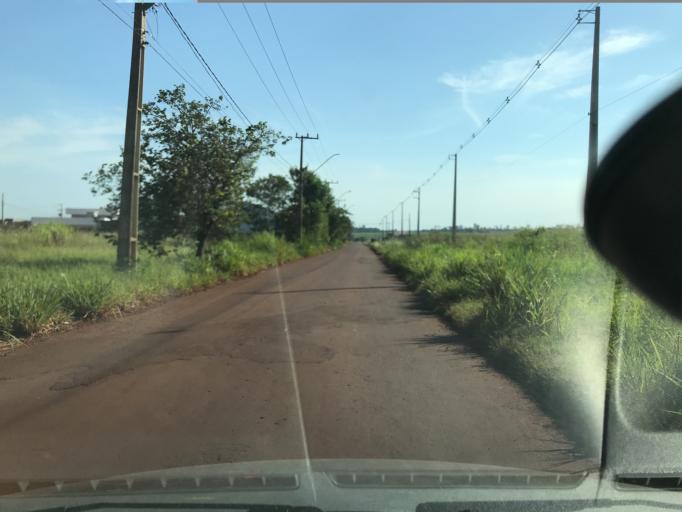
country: BR
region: Parana
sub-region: Palotina
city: Palotina
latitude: -24.2922
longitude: -53.8278
